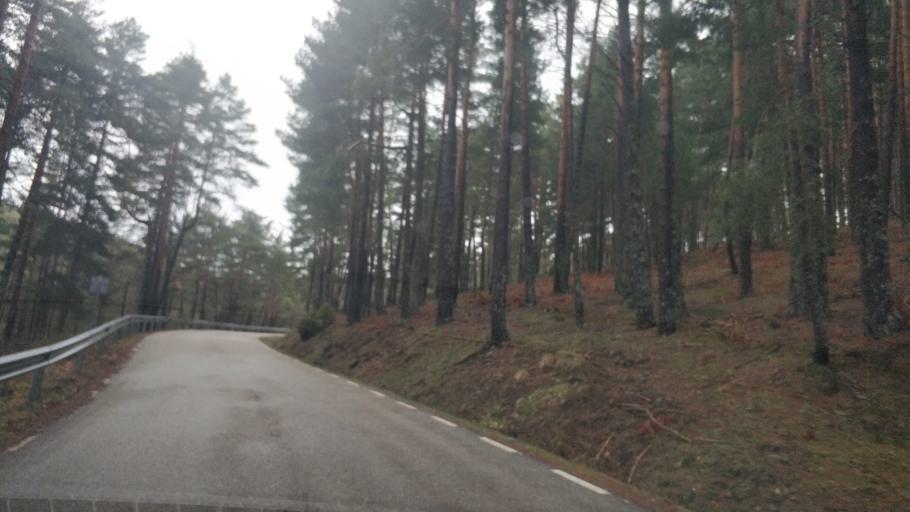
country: ES
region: Castille and Leon
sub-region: Provincia de Burgos
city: Neila
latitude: 42.0404
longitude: -3.0072
